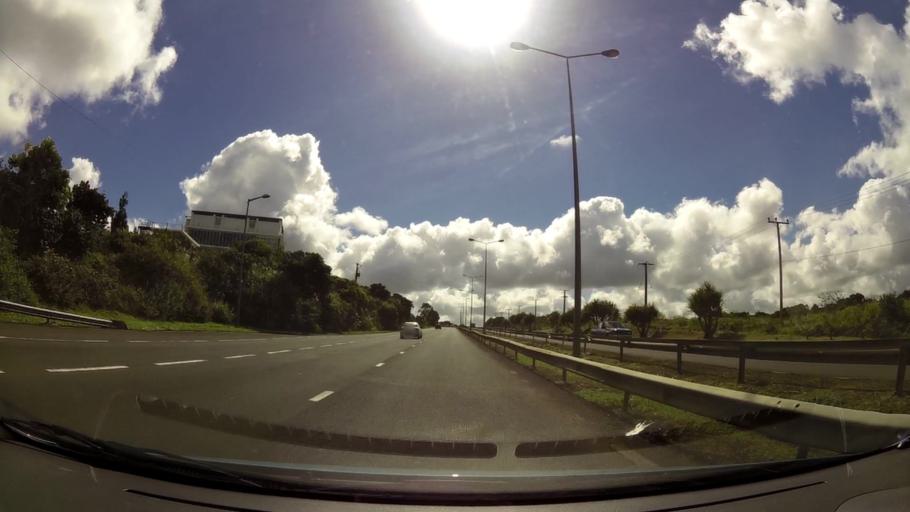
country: MU
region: Grand Port
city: Nouvelle France
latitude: -20.3877
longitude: 57.5735
